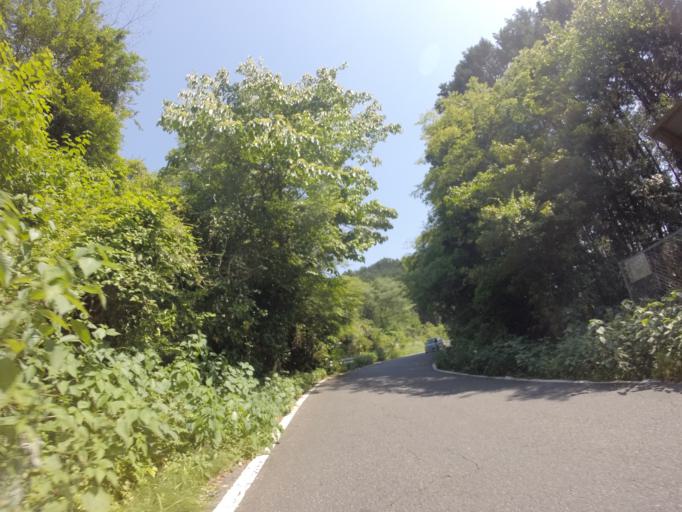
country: JP
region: Shizuoka
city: Fujinomiya
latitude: 35.1560
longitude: 138.5652
